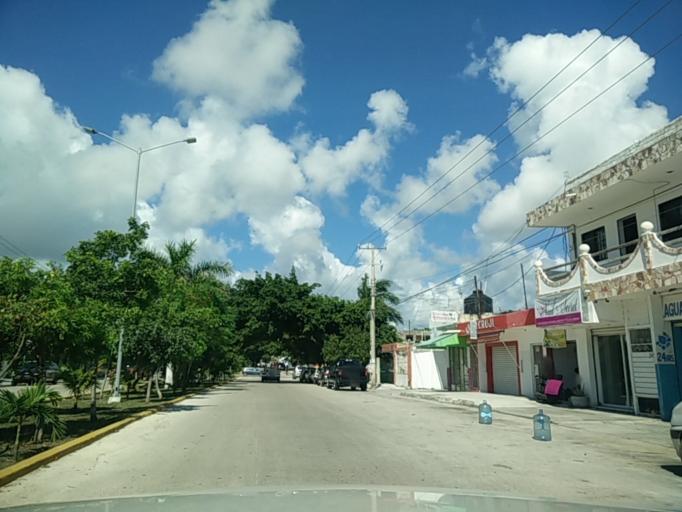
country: MX
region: Quintana Roo
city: Playa del Carmen
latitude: 20.6391
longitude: -87.0664
